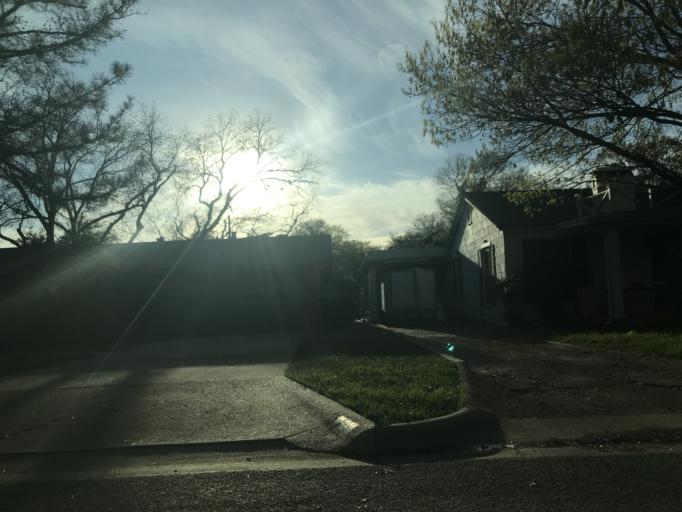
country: US
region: Texas
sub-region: Taylor County
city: Abilene
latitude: 32.4366
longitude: -99.7675
